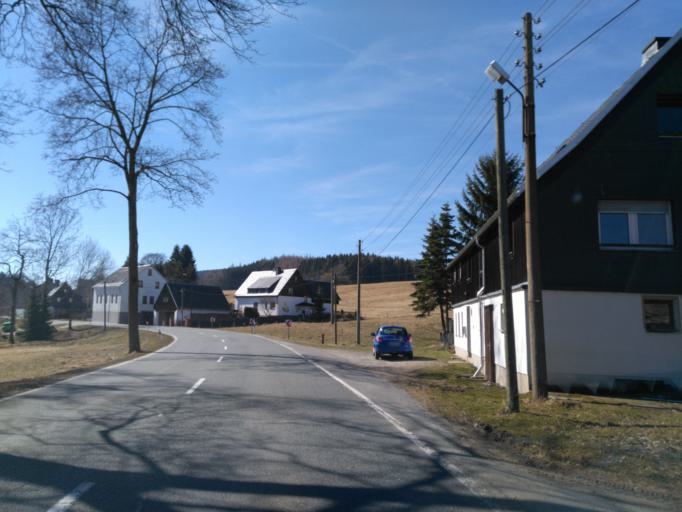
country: CZ
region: Ustecky
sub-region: Okres Chomutov
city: Vejprty
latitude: 50.4762
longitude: 13.0183
